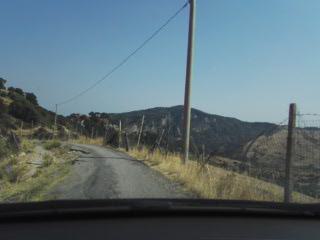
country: IT
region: Calabria
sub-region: Provincia di Reggio Calabria
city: Camini
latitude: 38.4488
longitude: 16.4649
